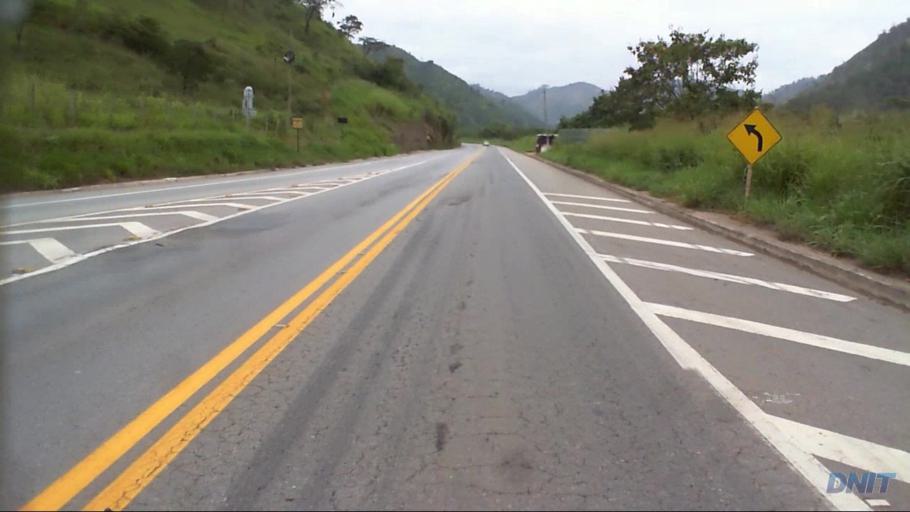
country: BR
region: Minas Gerais
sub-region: Timoteo
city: Timoteo
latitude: -19.5414
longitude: -42.6877
